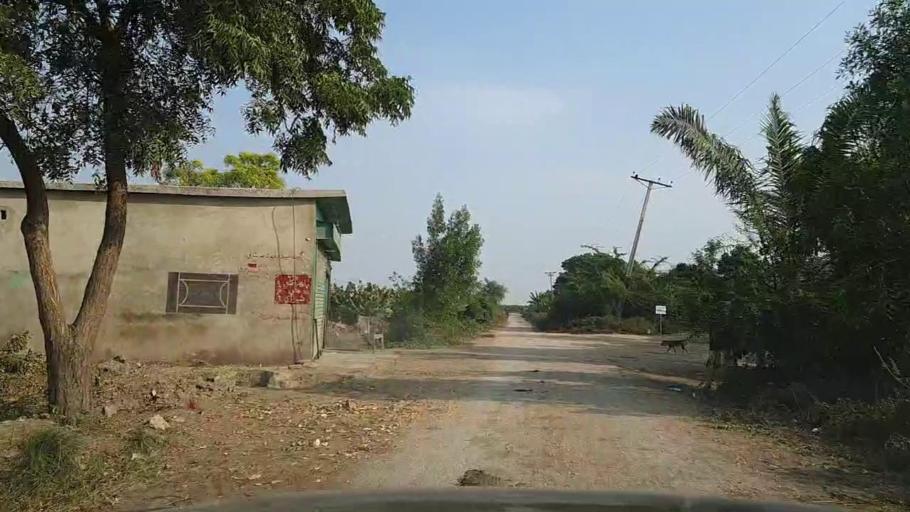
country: PK
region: Sindh
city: Thatta
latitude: 24.6450
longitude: 67.9387
